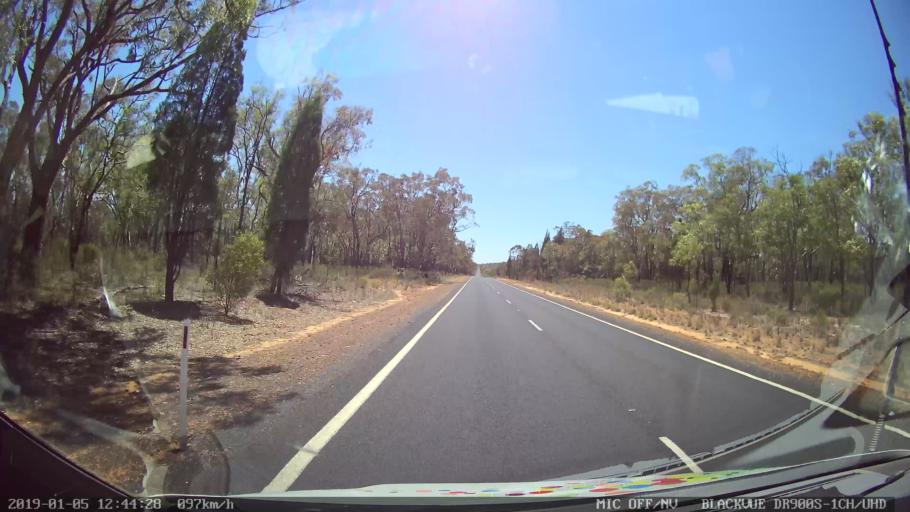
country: AU
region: New South Wales
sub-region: Warrumbungle Shire
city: Coonabarabran
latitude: -31.1374
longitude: 149.5377
